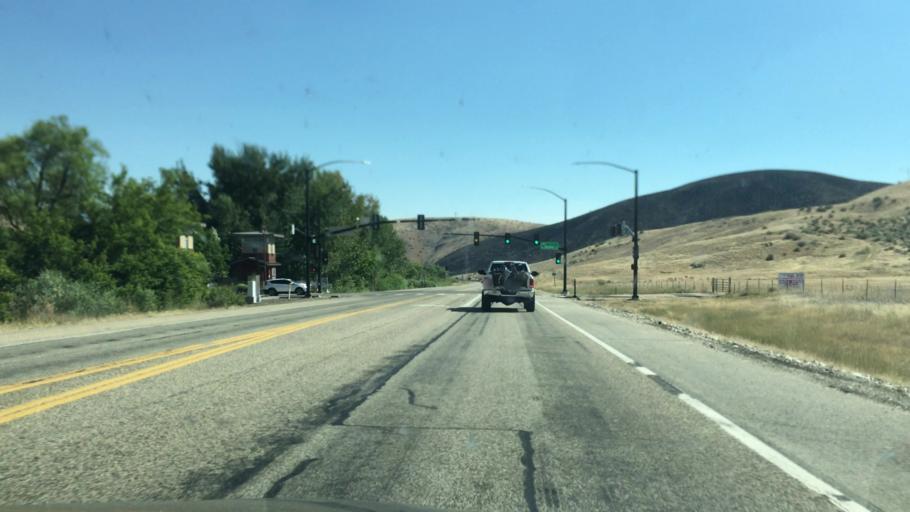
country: US
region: Idaho
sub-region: Ada County
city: Eagle
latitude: 43.7741
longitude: -116.2653
